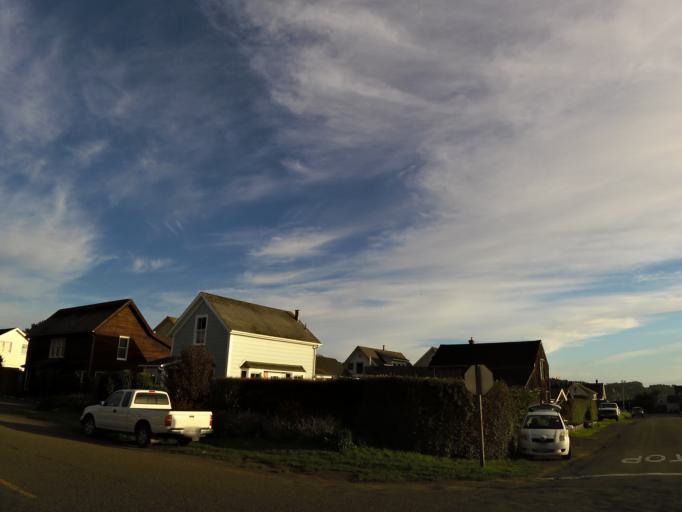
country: US
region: California
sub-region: Mendocino County
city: Fort Bragg
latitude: 39.3073
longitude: -123.8005
